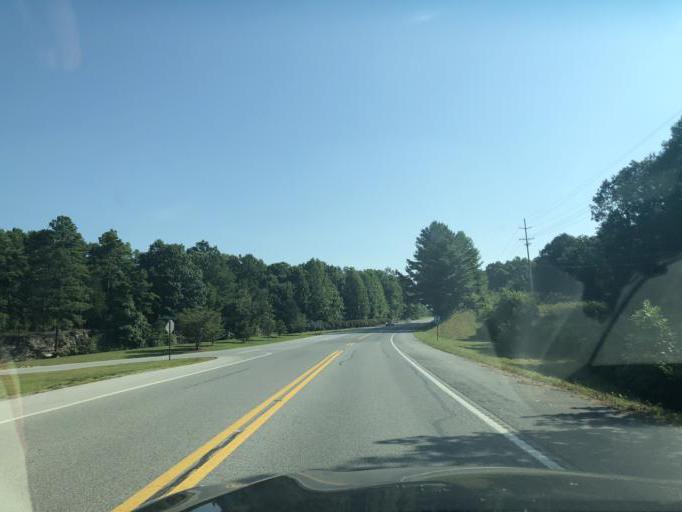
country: US
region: Tennessee
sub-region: Franklin County
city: Sewanee
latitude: 35.2074
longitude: -85.9021
